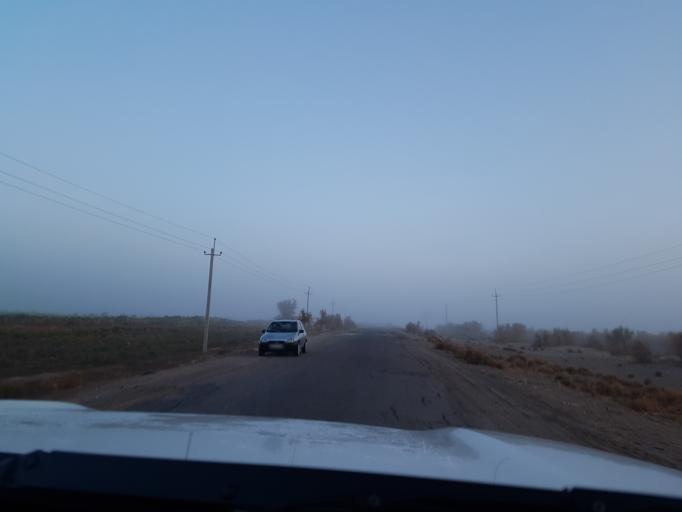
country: TM
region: Dasoguz
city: Koeneuergench
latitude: 41.7956
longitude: 58.6998
